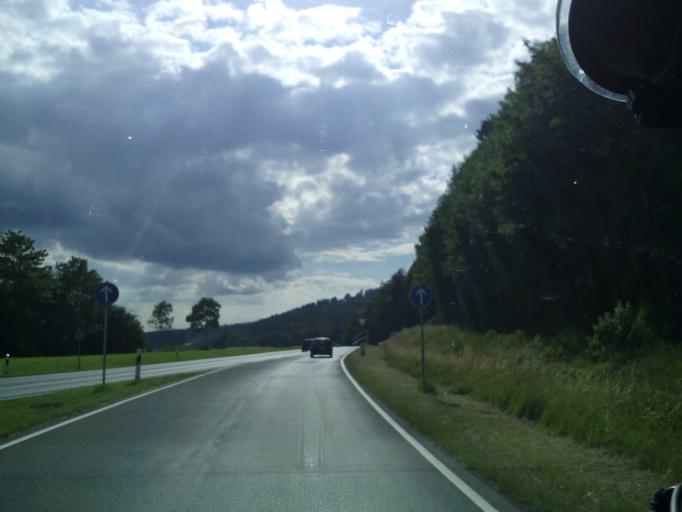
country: DE
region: Bavaria
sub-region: Upper Franconia
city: Neustadt bei Coburg
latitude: 50.3131
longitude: 11.0896
